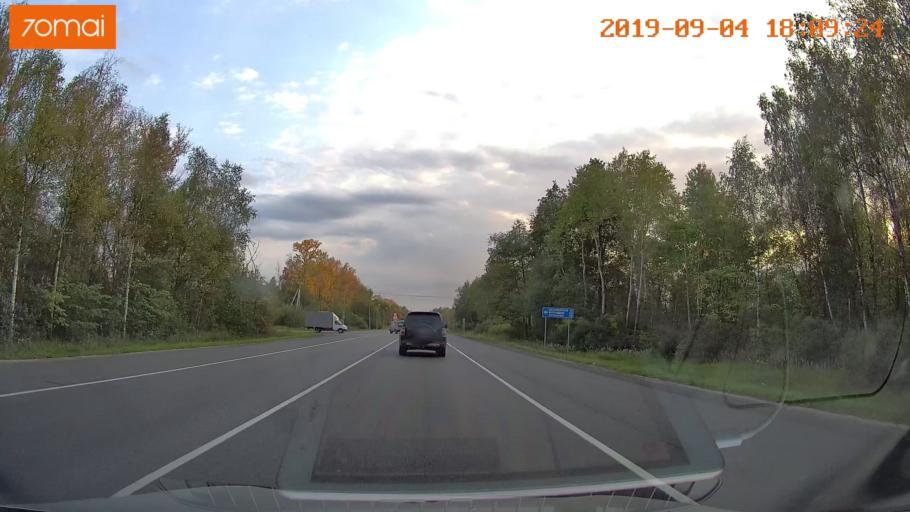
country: RU
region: Moskovskaya
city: Khorlovo
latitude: 55.3973
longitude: 38.7762
